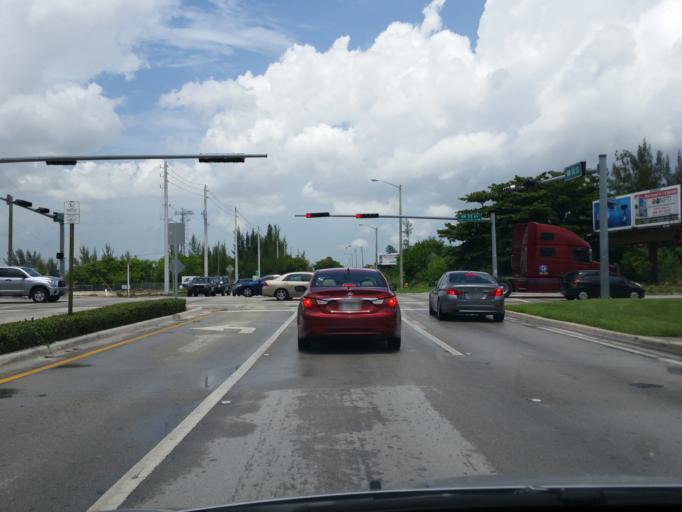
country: US
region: Florida
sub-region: Miami-Dade County
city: Sweetwater
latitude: 25.7861
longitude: -80.3758
